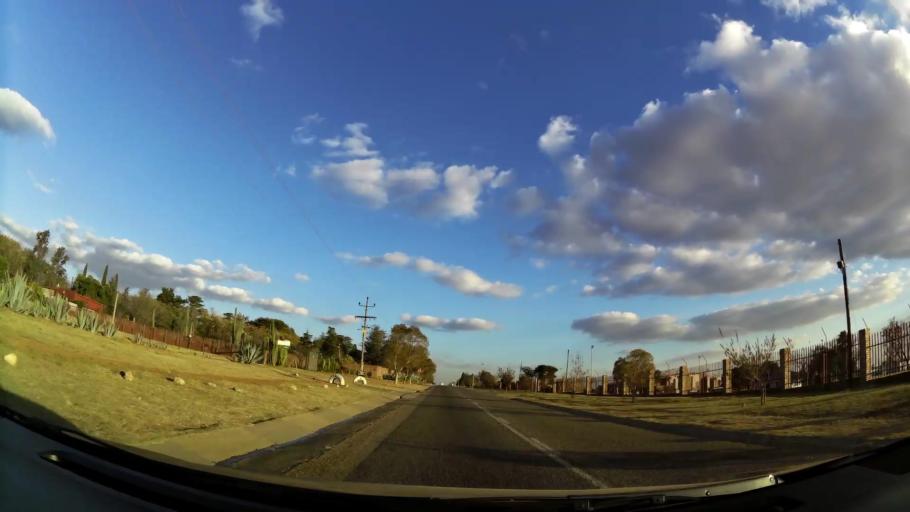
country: ZA
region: Gauteng
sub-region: City of Johannesburg Metropolitan Municipality
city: Midrand
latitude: -25.9549
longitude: 28.1541
